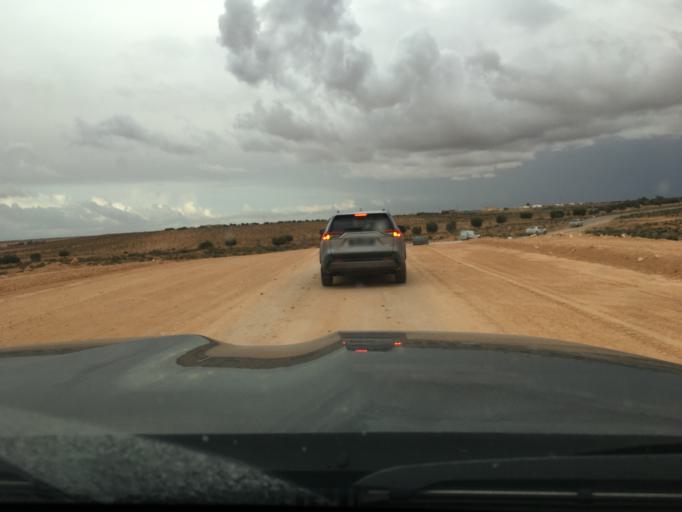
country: TN
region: Madanin
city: Medenine
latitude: 33.2864
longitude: 10.5999
